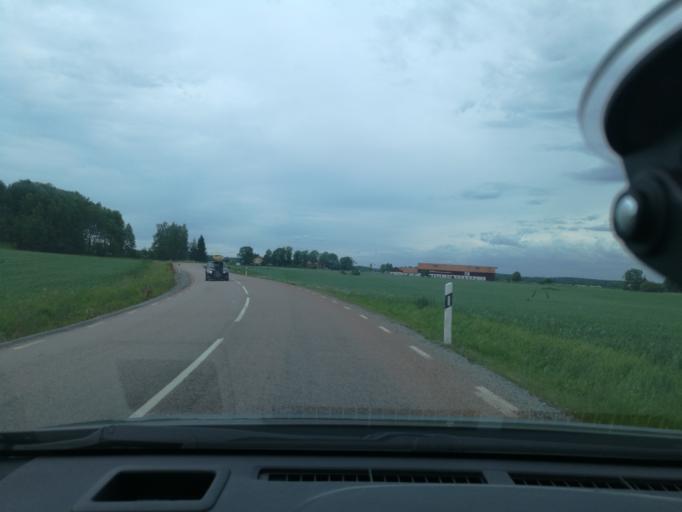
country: SE
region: Vaestmanland
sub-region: Vasteras
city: Skultuna
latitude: 59.7250
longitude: 16.4216
